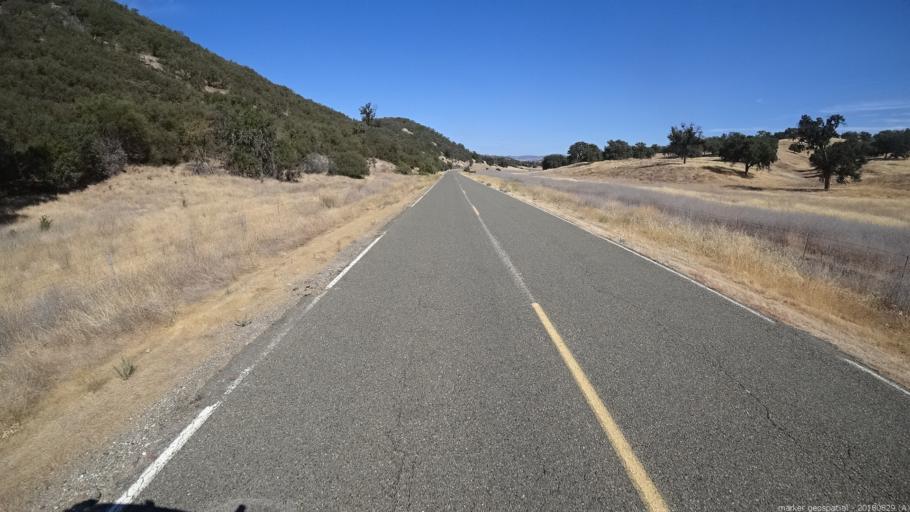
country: US
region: California
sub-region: San Luis Obispo County
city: Lake Nacimiento
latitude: 35.8747
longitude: -121.0648
